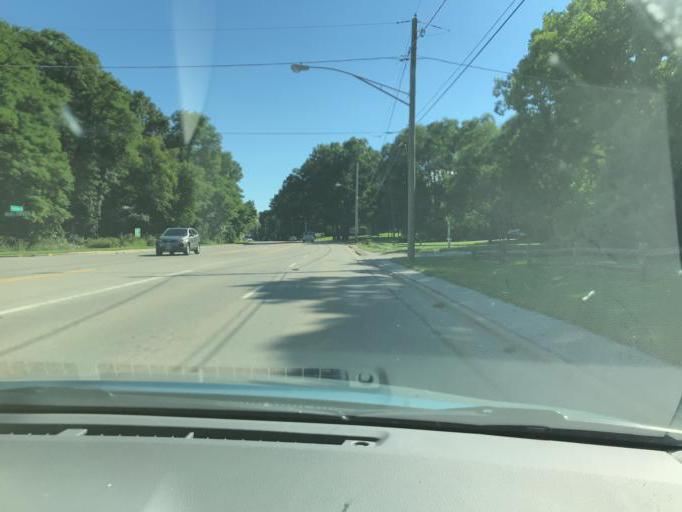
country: US
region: Illinois
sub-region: Lake County
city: Winthrop Harbor
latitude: 42.4721
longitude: -87.8249
